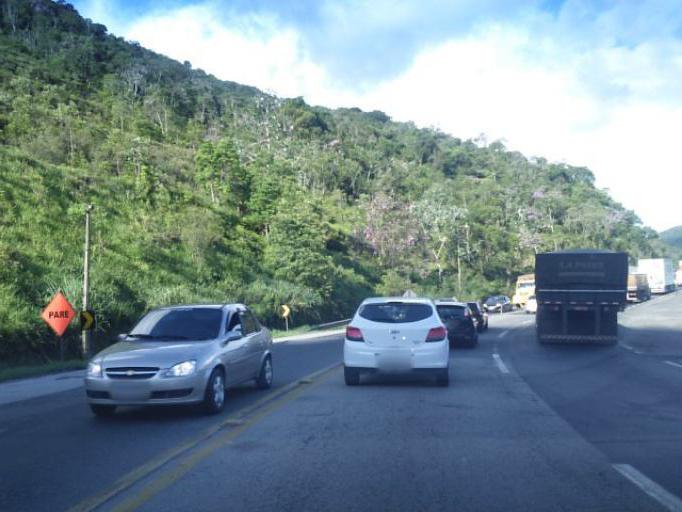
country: BR
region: Sao Paulo
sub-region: Miracatu
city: Miracatu
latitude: -24.1092
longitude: -47.2688
